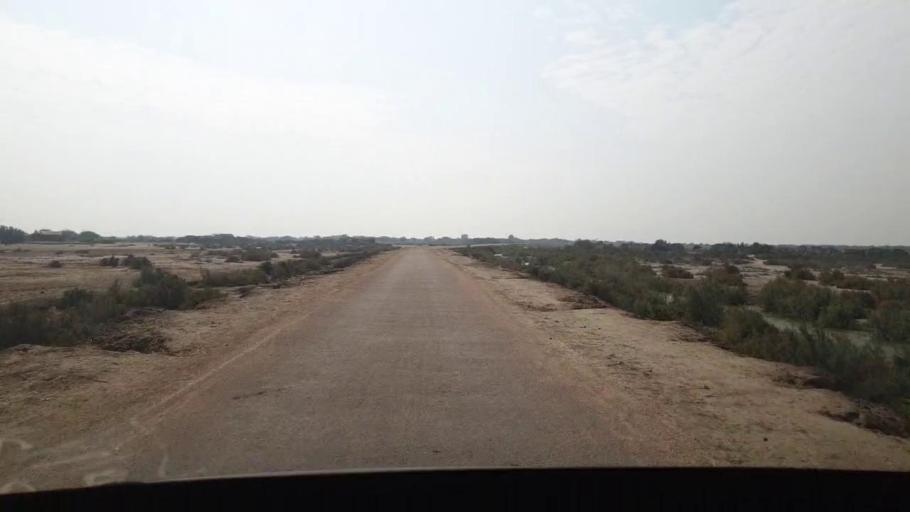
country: PK
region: Sindh
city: Chuhar Jamali
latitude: 24.2443
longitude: 67.9905
